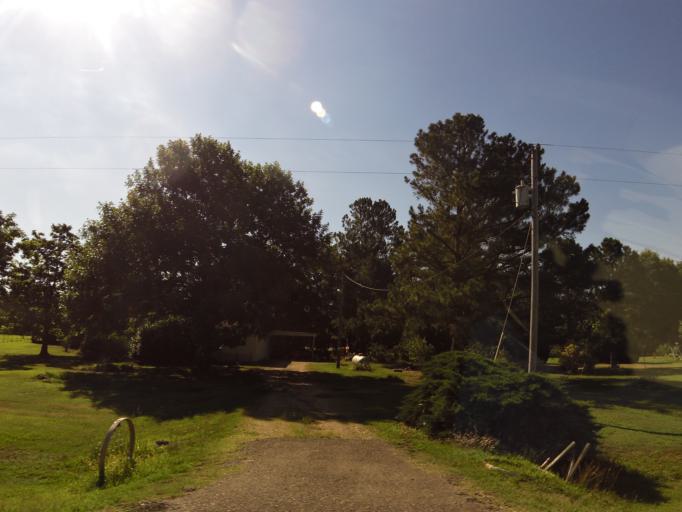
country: US
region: Arkansas
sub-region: Clay County
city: Corning
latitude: 36.4097
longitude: -90.4983
